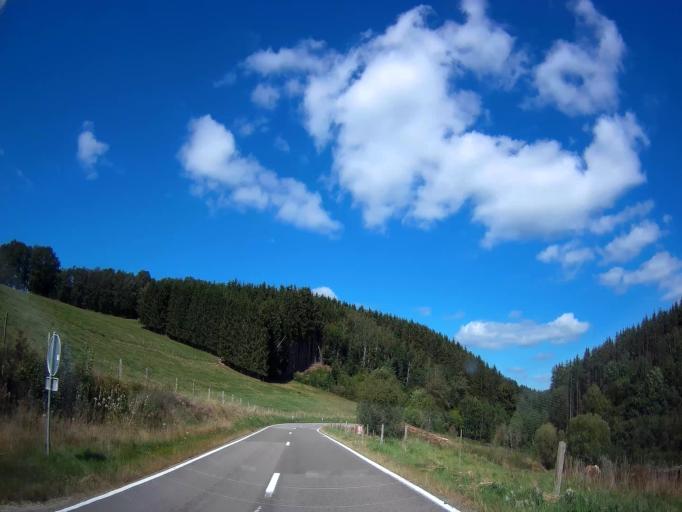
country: BE
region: Wallonia
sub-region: Province du Luxembourg
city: Bertogne
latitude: 50.0930
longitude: 5.6746
